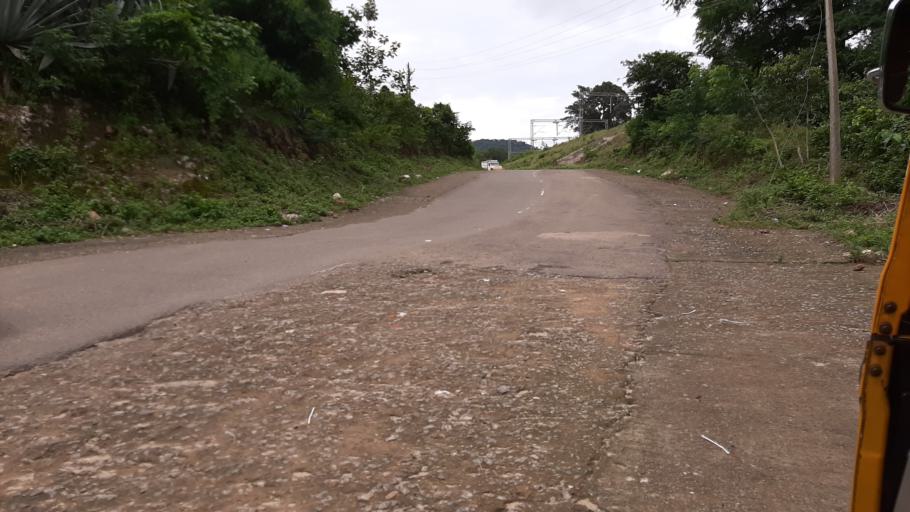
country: IN
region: Andhra Pradesh
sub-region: Vizianagaram District
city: Salur
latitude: 18.2772
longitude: 83.0374
